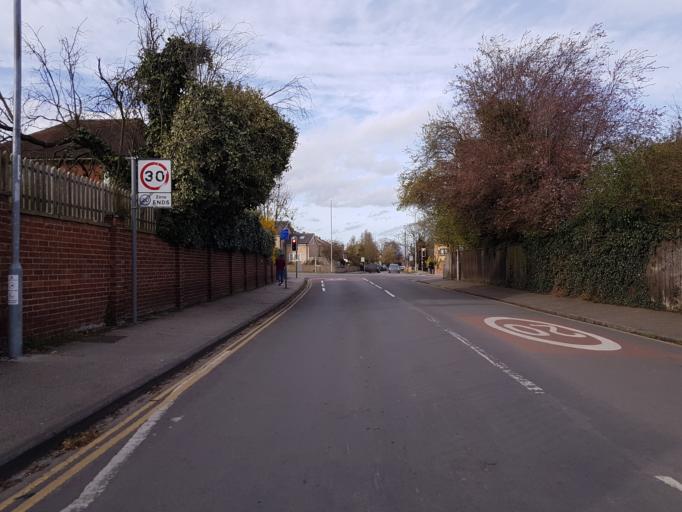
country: GB
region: England
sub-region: Cambridgeshire
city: Cambridge
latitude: 52.2205
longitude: 0.1184
